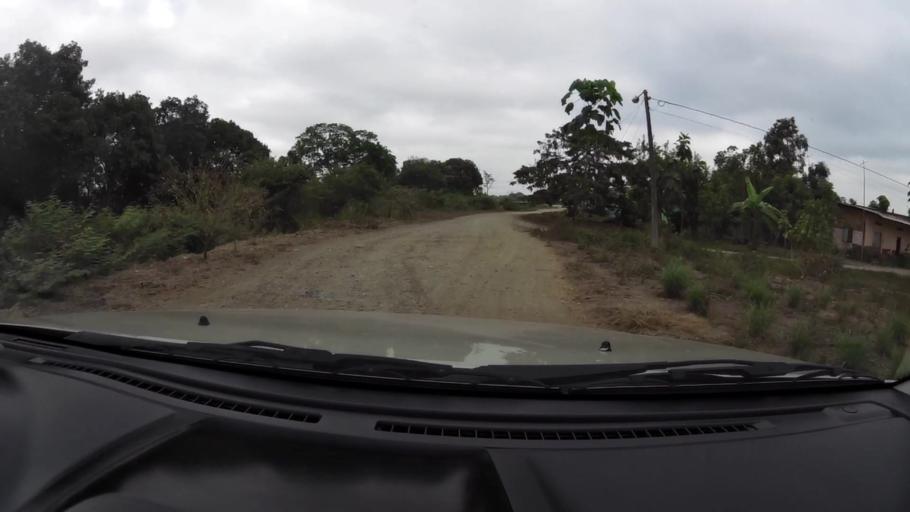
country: EC
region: Guayas
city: Yaguachi Nuevo
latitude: -2.2446
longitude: -79.6436
